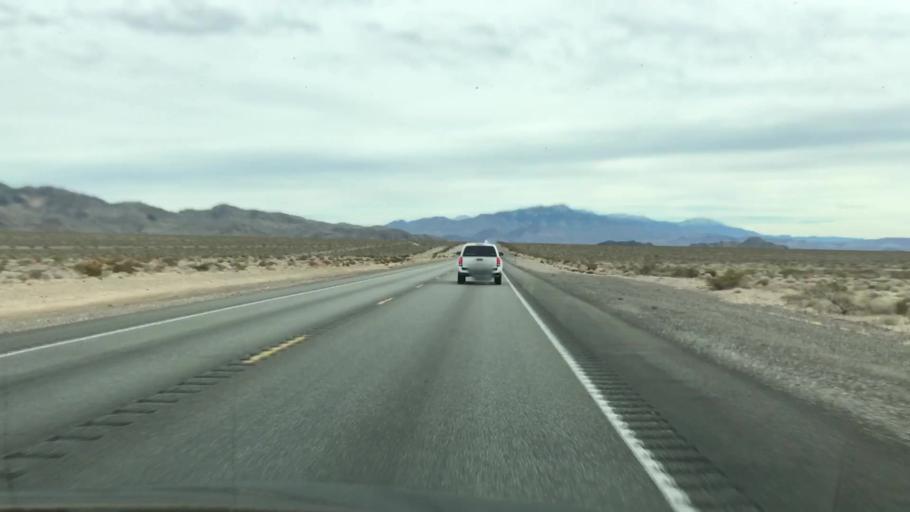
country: US
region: Nevada
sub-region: Nye County
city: Pahrump
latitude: 36.6087
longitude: -116.2665
